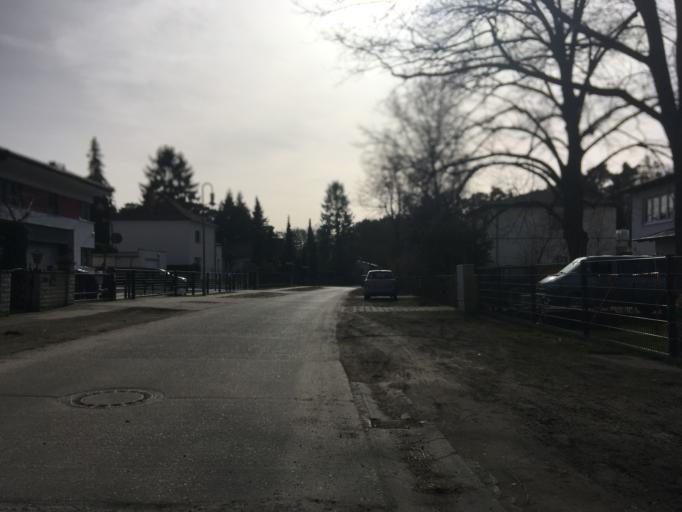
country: DE
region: Berlin
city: Schmockwitz
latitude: 52.3914
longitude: 13.6303
